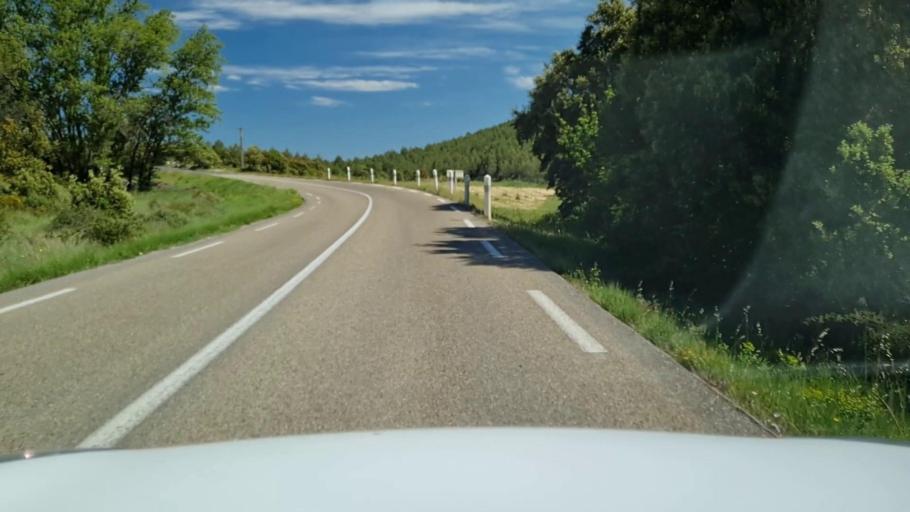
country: FR
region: Languedoc-Roussillon
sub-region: Departement du Gard
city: Villevieille
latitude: 43.8544
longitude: 4.0968
